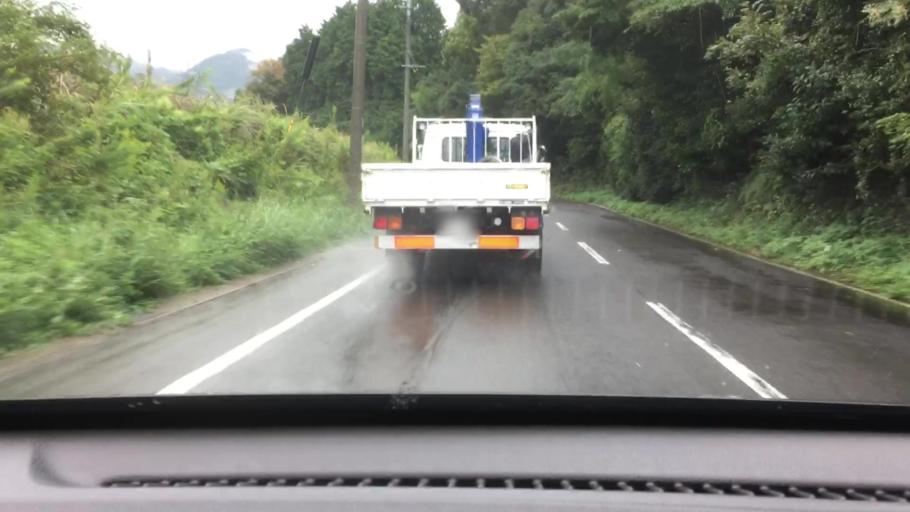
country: JP
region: Nagasaki
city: Togitsu
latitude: 32.8591
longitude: 129.7775
